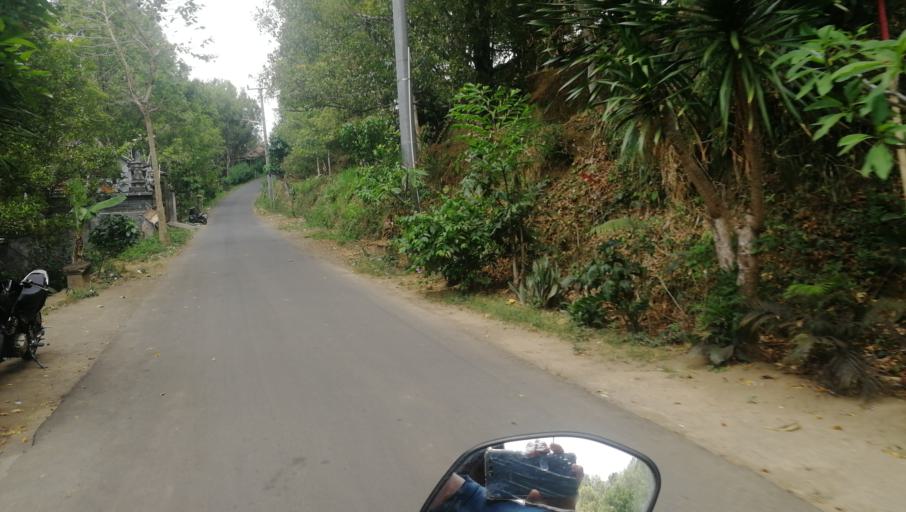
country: ID
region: Bali
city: Munduk
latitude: -8.2842
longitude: 115.0364
